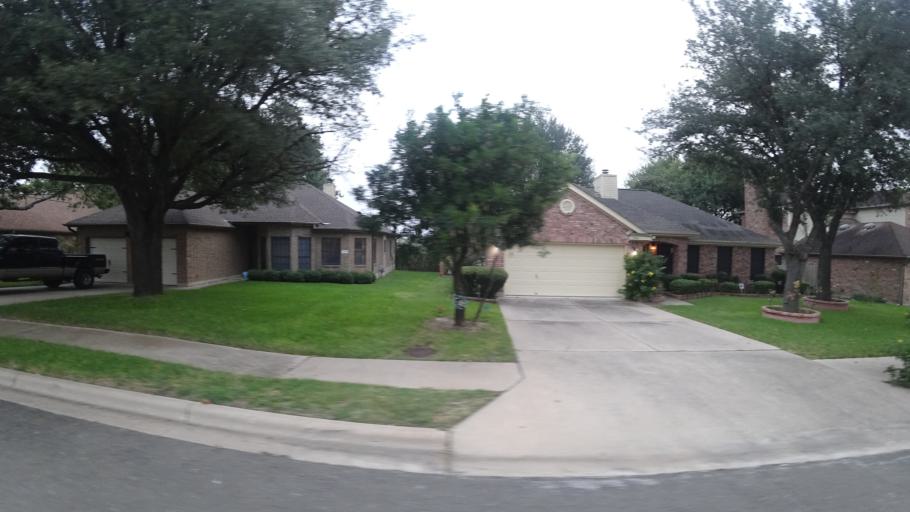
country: US
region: Texas
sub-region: Travis County
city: Wells Branch
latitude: 30.3687
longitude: -97.6696
